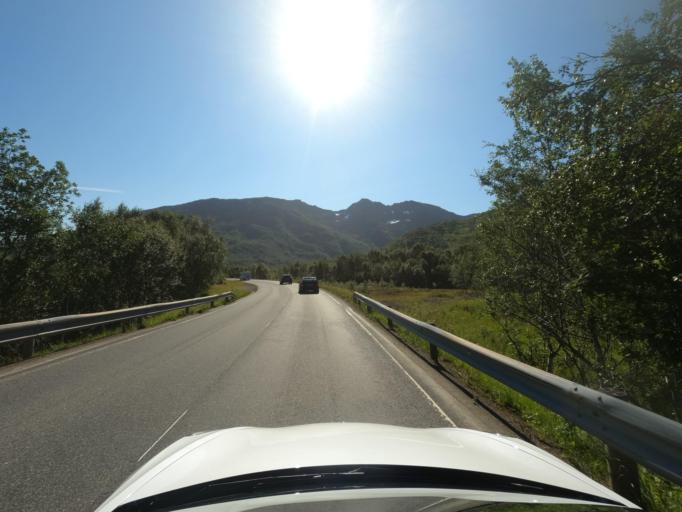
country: NO
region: Nordland
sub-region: Lodingen
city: Lodingen
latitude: 68.5310
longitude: 15.7283
